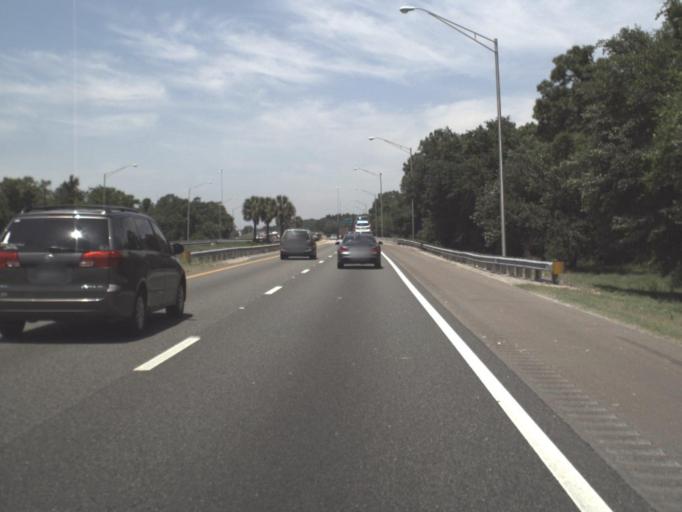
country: US
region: Florida
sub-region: Duval County
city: Jacksonville
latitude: 30.4274
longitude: -81.5729
